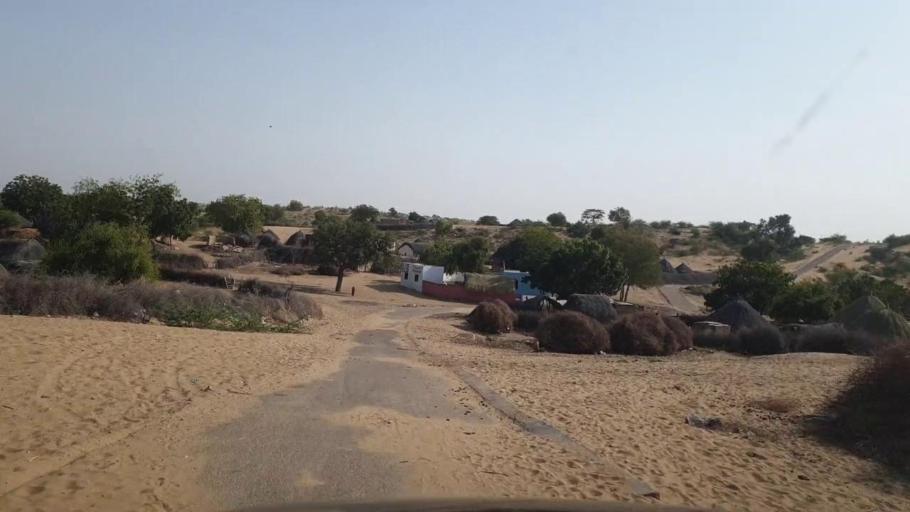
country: PK
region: Sindh
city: Islamkot
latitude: 25.1203
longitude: 70.5124
